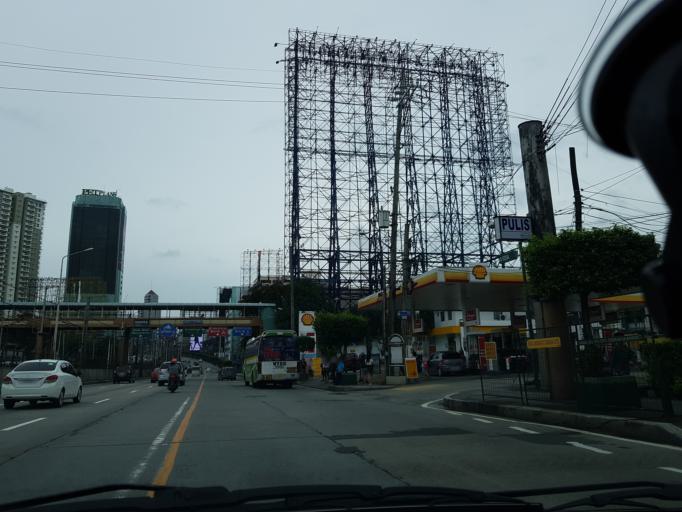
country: PH
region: Metro Manila
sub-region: Makati City
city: Makati City
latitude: 14.5598
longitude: 121.0409
